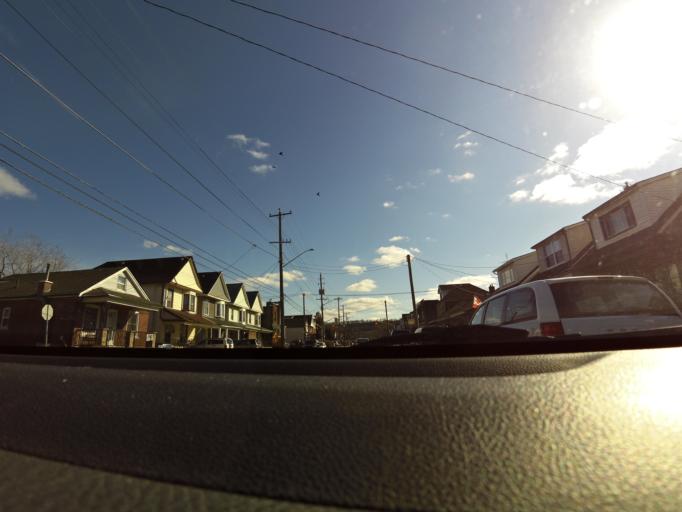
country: CA
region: Ontario
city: Hamilton
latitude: 43.2506
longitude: -79.8288
